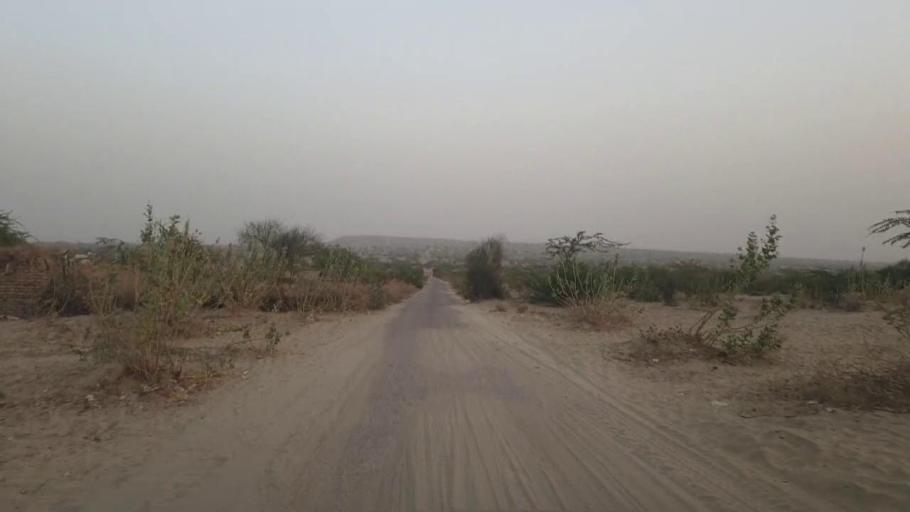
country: PK
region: Sindh
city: Chor
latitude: 25.5115
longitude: 69.8154
